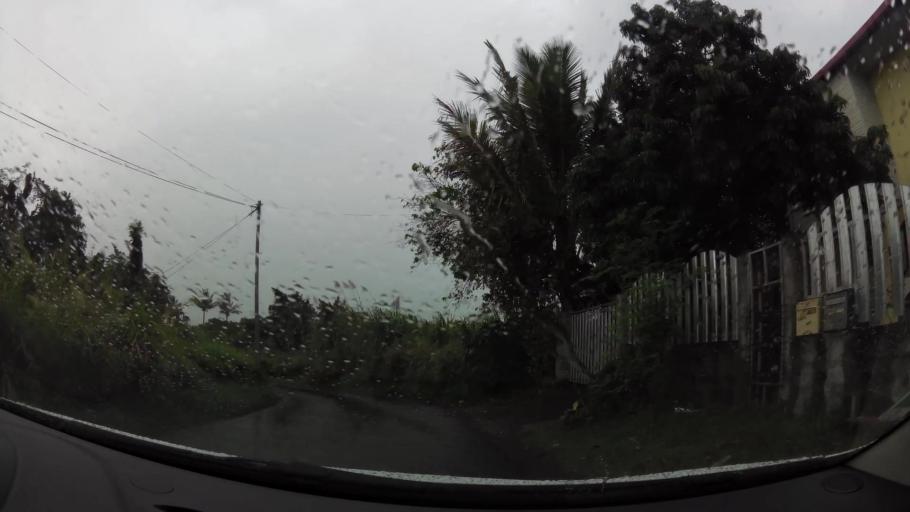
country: RE
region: Reunion
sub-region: Reunion
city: Saint-Andre
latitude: -20.9719
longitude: 55.6604
